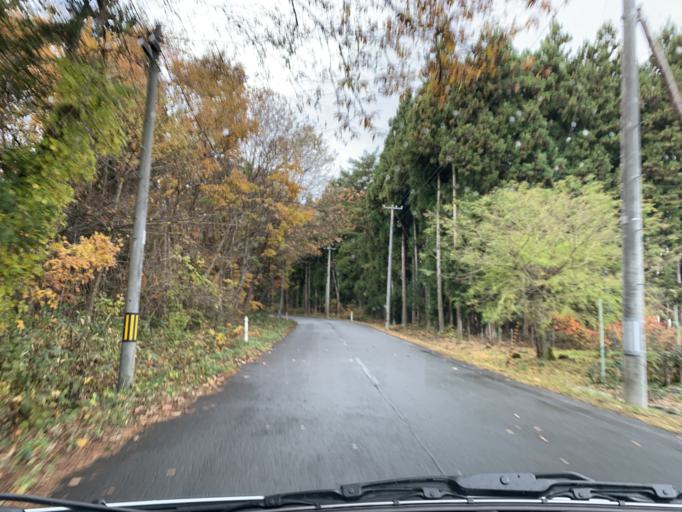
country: JP
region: Iwate
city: Mizusawa
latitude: 39.1026
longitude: 140.9939
